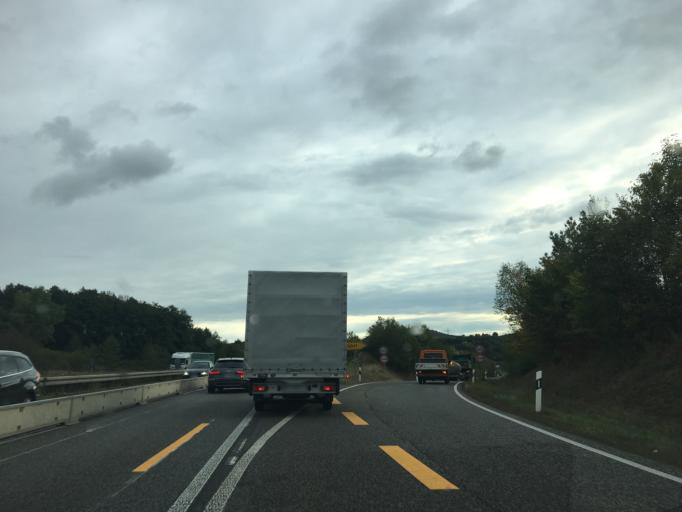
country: DE
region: Hesse
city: Staufenberg
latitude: 50.6691
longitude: 8.7215
